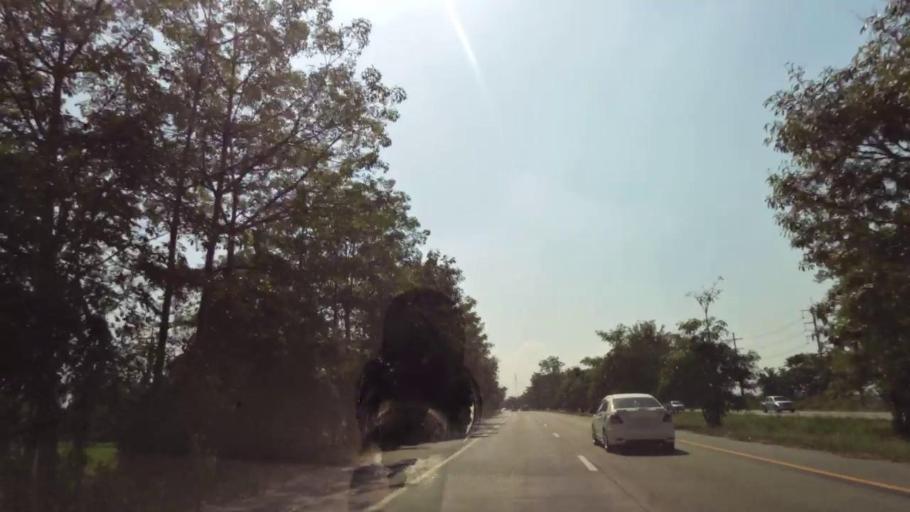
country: TH
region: Phitsanulok
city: Bang Rakam
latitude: 16.6446
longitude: 100.1501
